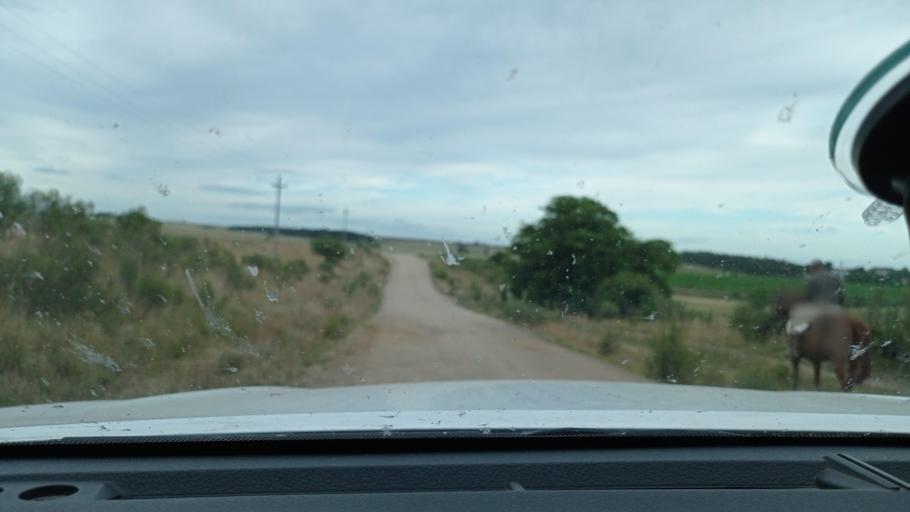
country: UY
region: Florida
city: Casupa
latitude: -34.1024
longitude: -55.7467
